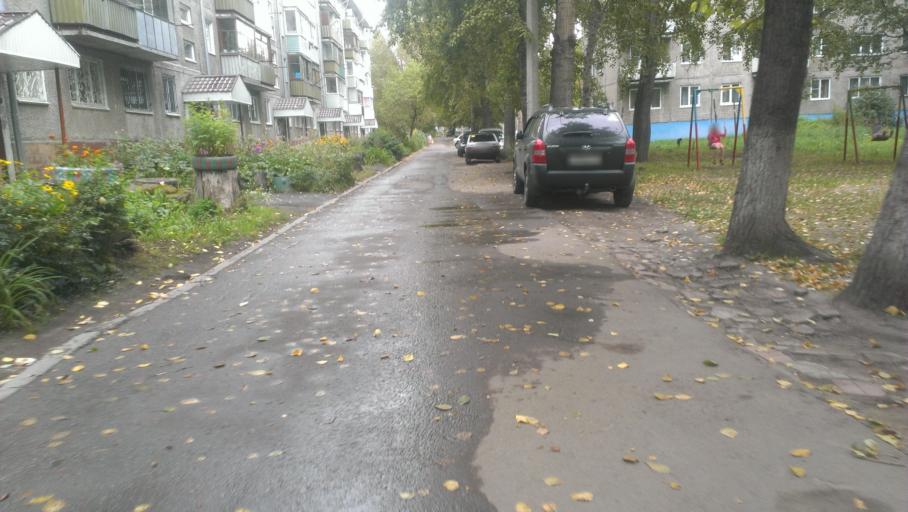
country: RU
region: Altai Krai
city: Novosilikatnyy
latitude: 53.3730
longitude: 83.6730
